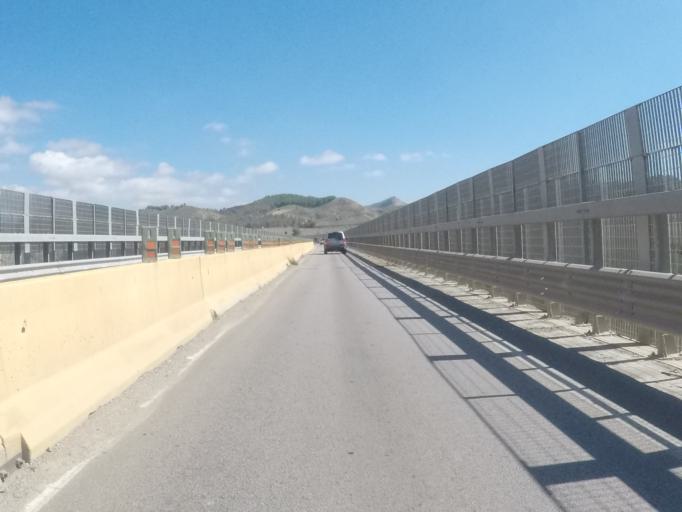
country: IT
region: Sicily
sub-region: Enna
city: Villarosa
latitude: 37.5381
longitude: 14.1318
